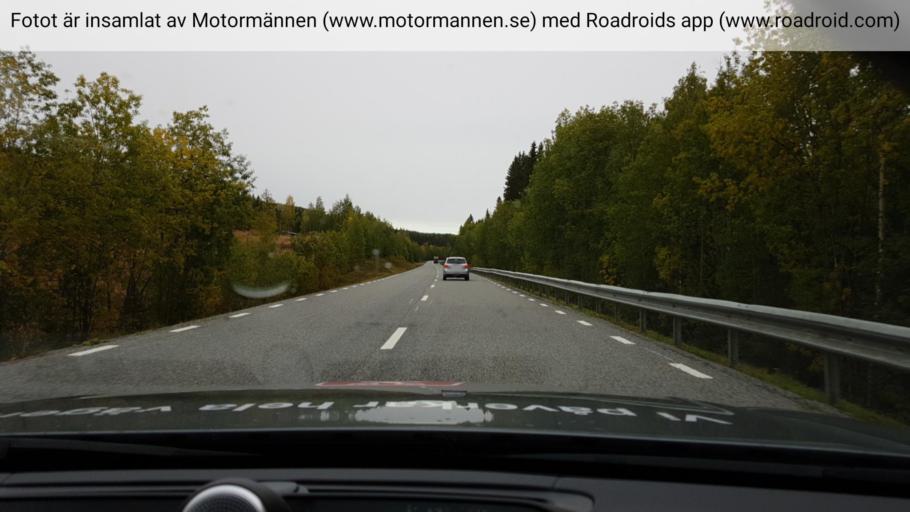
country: SE
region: Jaemtland
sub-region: Stroemsunds Kommun
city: Stroemsund
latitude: 64.0616
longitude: 15.5529
